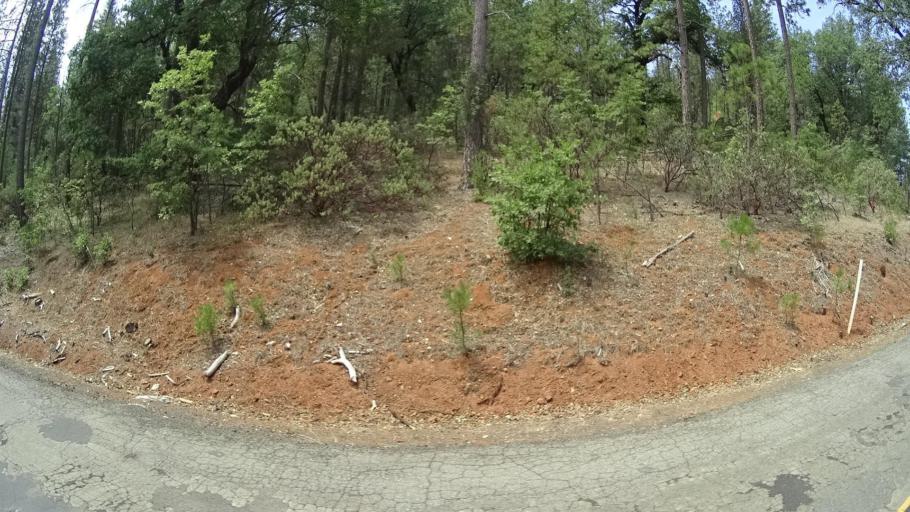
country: US
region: California
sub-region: Mariposa County
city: Midpines
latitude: 37.7493
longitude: -120.0394
